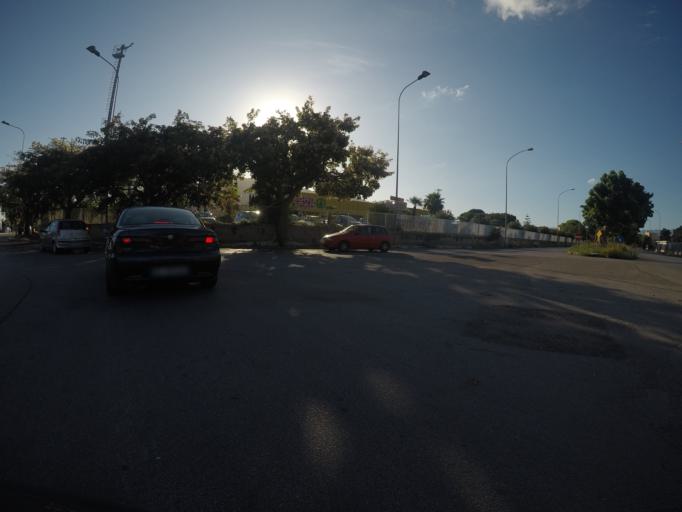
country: IT
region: Sicily
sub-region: Palermo
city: Palermo
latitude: 38.1887
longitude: 13.3150
